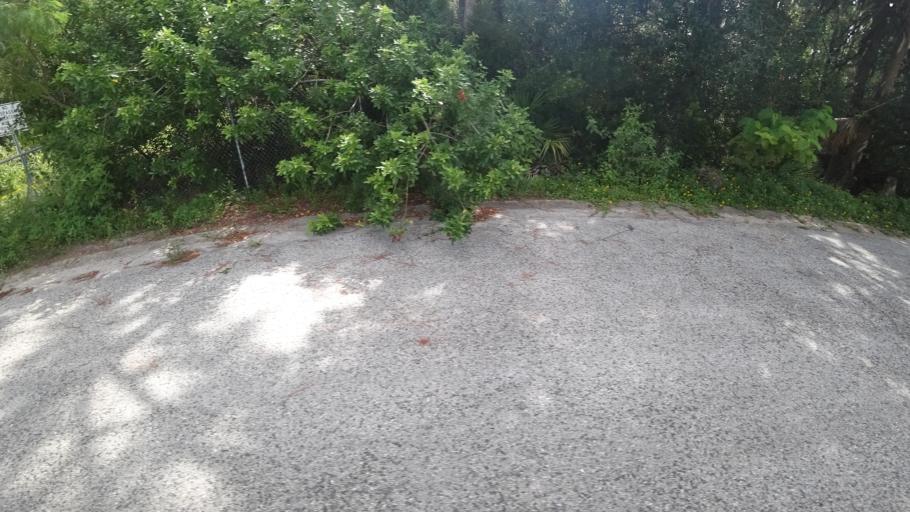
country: US
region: Florida
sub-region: Manatee County
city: Samoset
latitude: 27.4573
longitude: -82.4554
